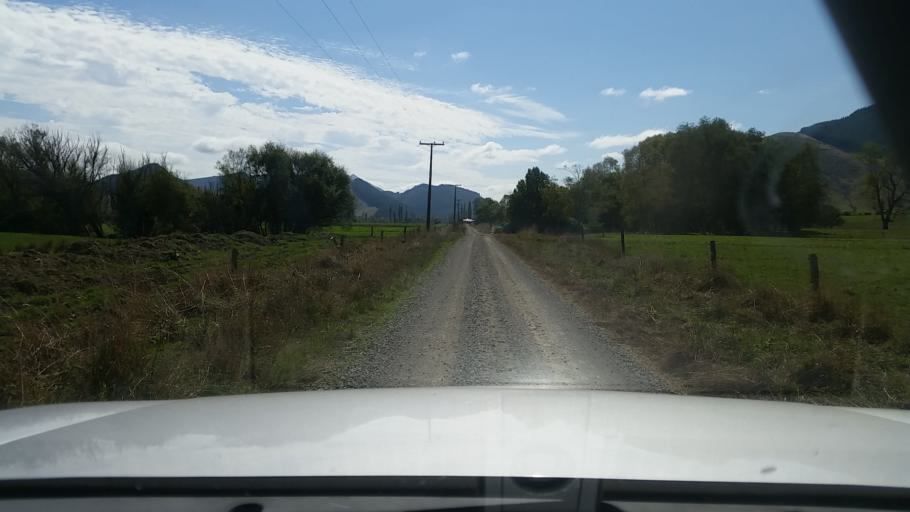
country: NZ
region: Nelson
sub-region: Nelson City
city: Nelson
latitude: -41.2548
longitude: 173.5825
